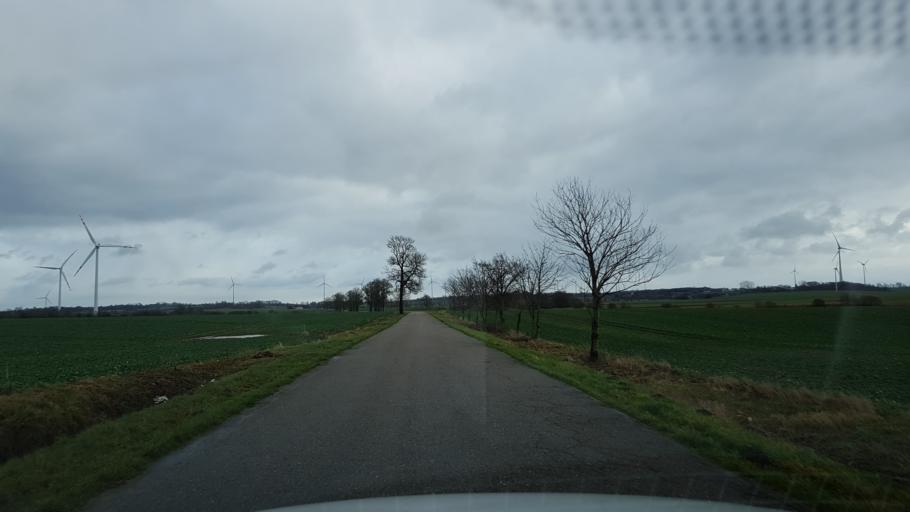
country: PL
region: West Pomeranian Voivodeship
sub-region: Powiat slawienski
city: Slawno
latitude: 54.5185
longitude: 16.6629
